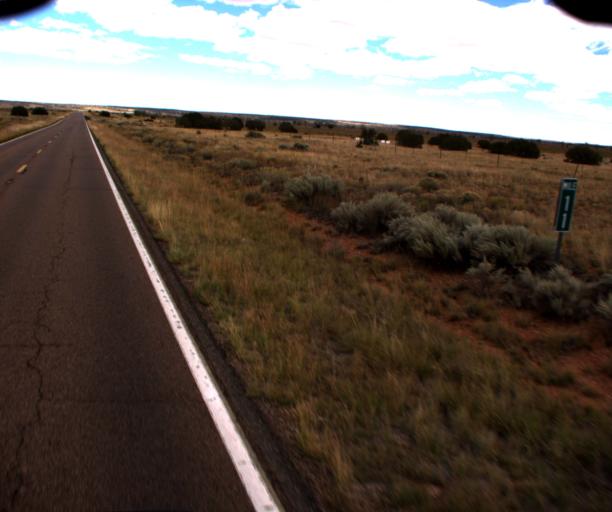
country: US
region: Arizona
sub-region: Navajo County
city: Heber-Overgaard
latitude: 34.6005
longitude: -110.3878
